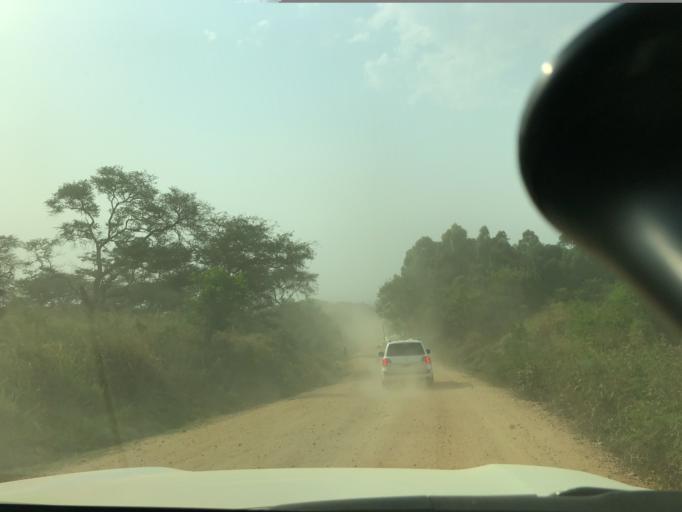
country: UG
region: Western Region
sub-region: Kasese District
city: Kilembe
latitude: 0.0560
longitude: 29.6688
